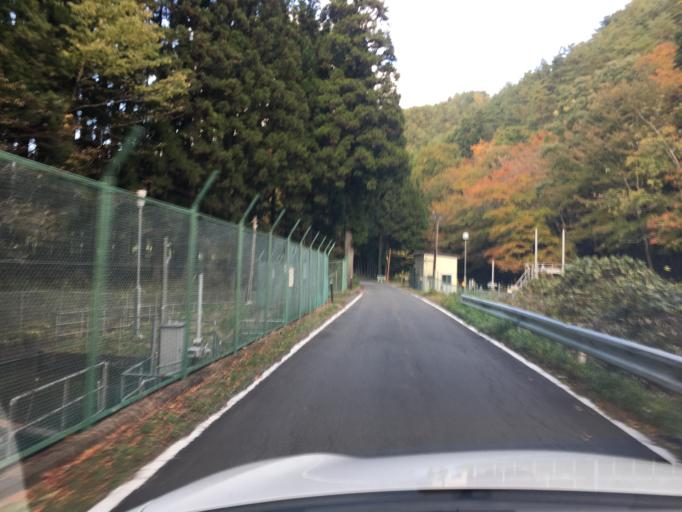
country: JP
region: Fukushima
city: Iwaki
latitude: 37.2220
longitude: 140.7586
